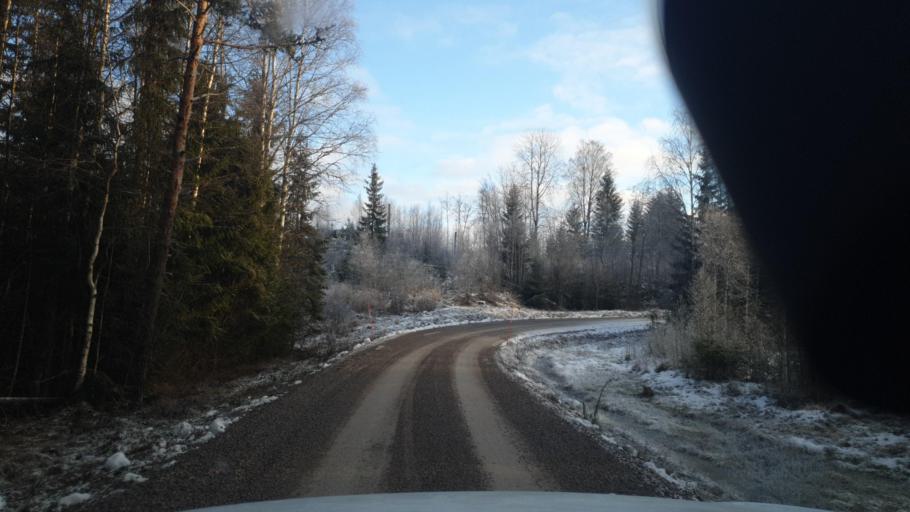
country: SE
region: Vaermland
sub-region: Eda Kommun
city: Charlottenberg
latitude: 60.0907
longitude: 12.5026
